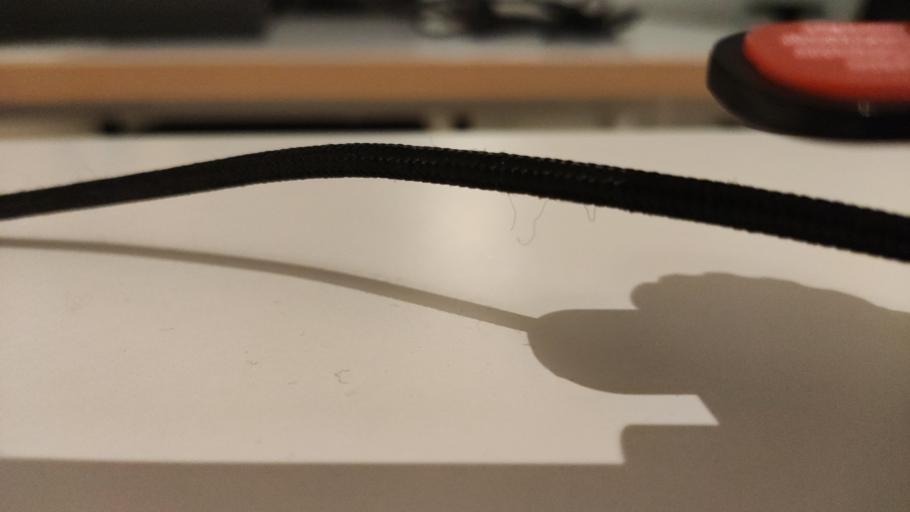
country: RU
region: Moskovskaya
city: Kurovskoye
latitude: 55.5770
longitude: 38.8881
